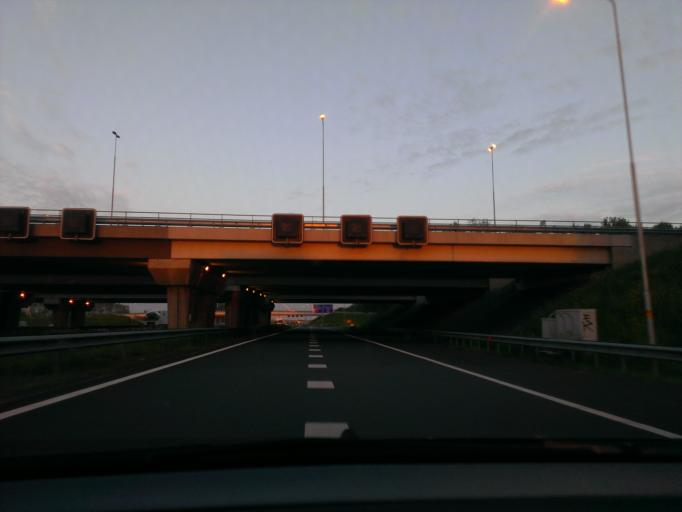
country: NL
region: Gelderland
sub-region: Gemeente Overbetuwe
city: Herveld
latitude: 51.9084
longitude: 5.7667
